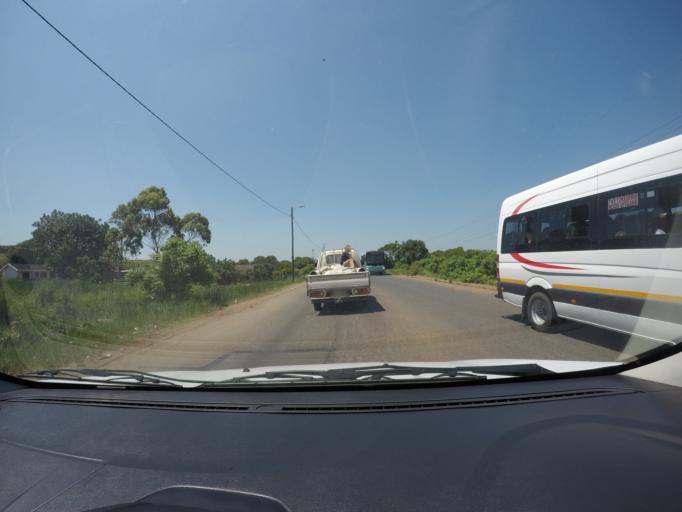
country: ZA
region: KwaZulu-Natal
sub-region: uThungulu District Municipality
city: eSikhawini
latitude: -28.8371
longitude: 31.9375
